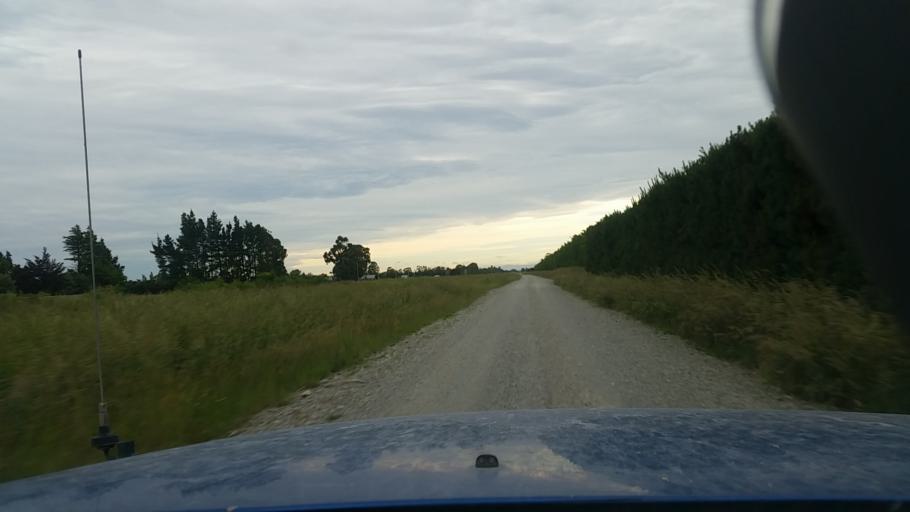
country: NZ
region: Canterbury
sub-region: Ashburton District
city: Tinwald
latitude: -43.9361
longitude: 171.6893
